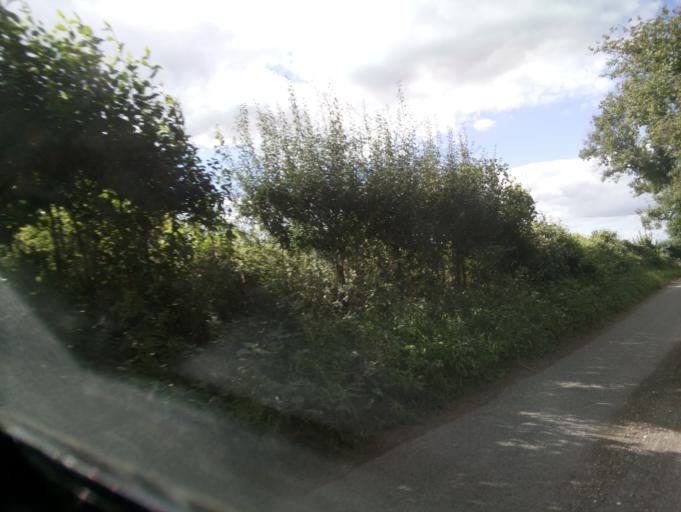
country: GB
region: England
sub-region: Hampshire
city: Chandlers Ford
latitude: 51.0691
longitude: -1.3805
